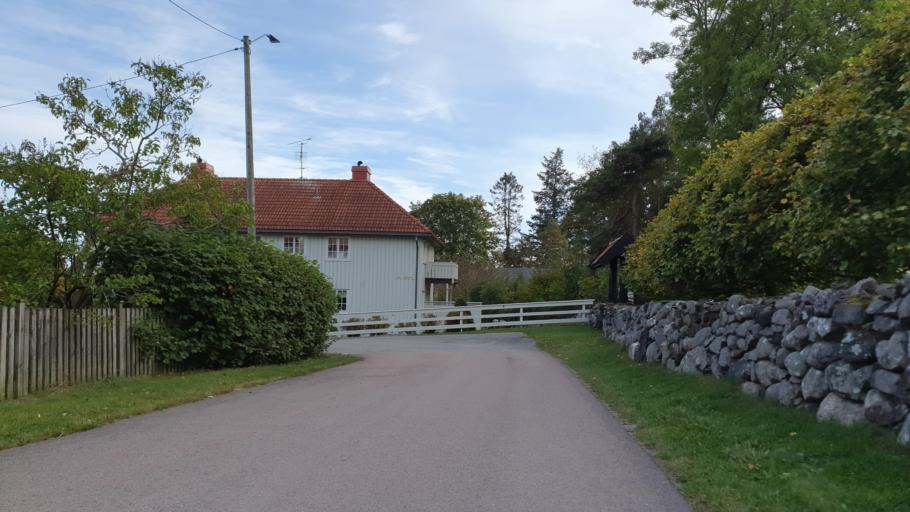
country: NO
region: Vestfold
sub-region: Tonsberg
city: Tonsberg
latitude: 59.2793
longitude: 10.4175
